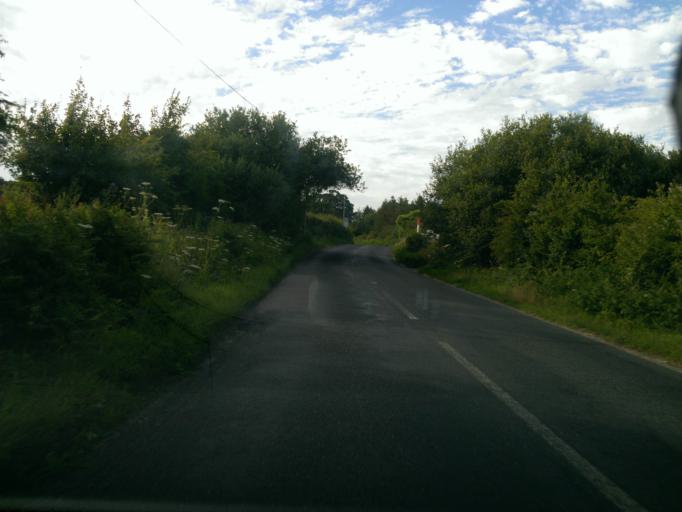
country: GB
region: England
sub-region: Essex
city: Great Bentley
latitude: 51.8365
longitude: 1.0720
